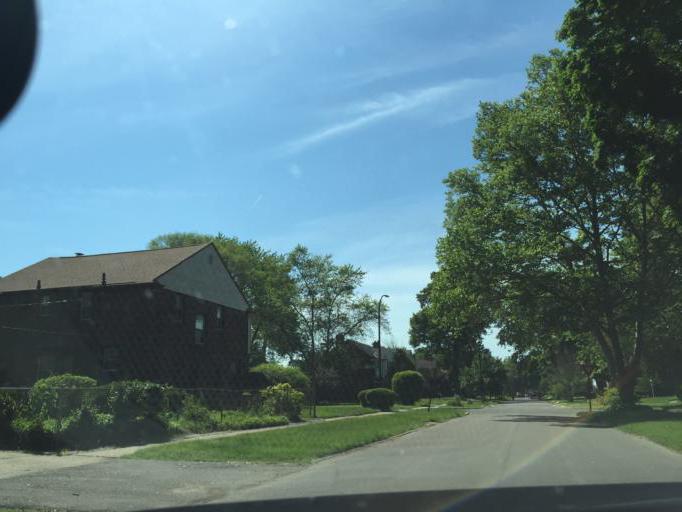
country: US
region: Michigan
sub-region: Oakland County
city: Oak Park
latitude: 42.4039
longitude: -83.2237
